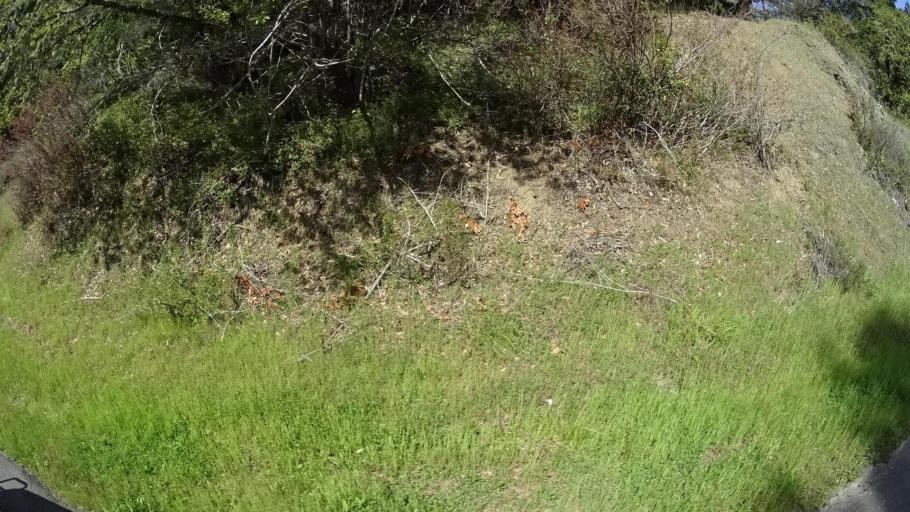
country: US
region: California
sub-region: Humboldt County
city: Redway
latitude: 40.4333
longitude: -123.7678
